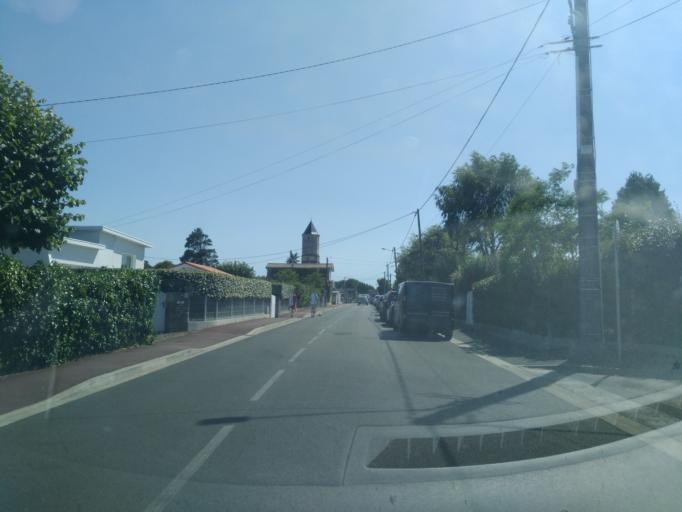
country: FR
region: Poitou-Charentes
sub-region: Departement de la Charente-Maritime
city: Saint-Palais-sur-Mer
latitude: 45.6444
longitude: -1.0815
